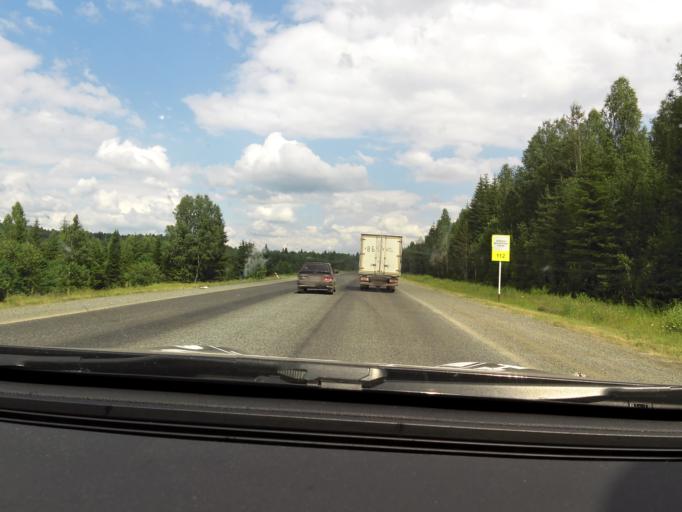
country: RU
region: Sverdlovsk
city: Arti
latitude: 56.7907
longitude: 58.4449
